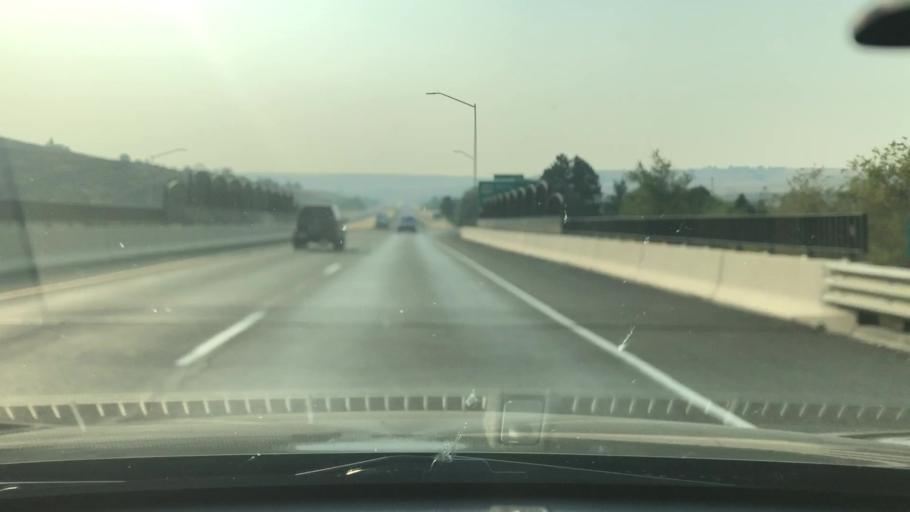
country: US
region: Oregon
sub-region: Umatilla County
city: Pendleton
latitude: 45.6630
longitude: -118.8058
